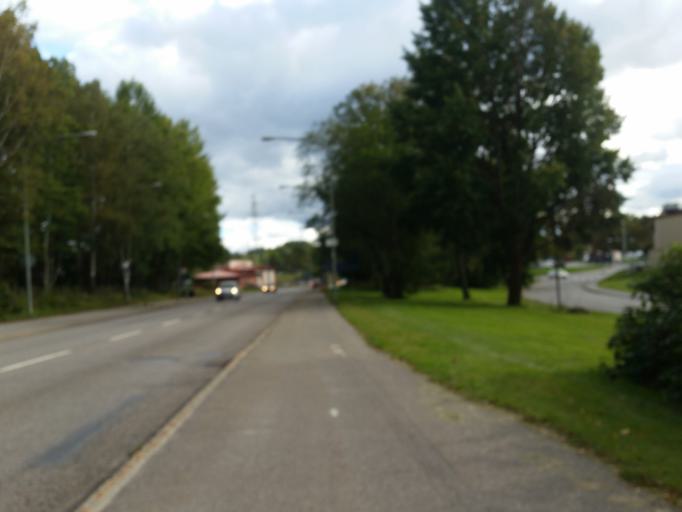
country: SE
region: Stockholm
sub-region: Nacka Kommun
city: Alta
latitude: 59.2649
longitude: 18.1215
